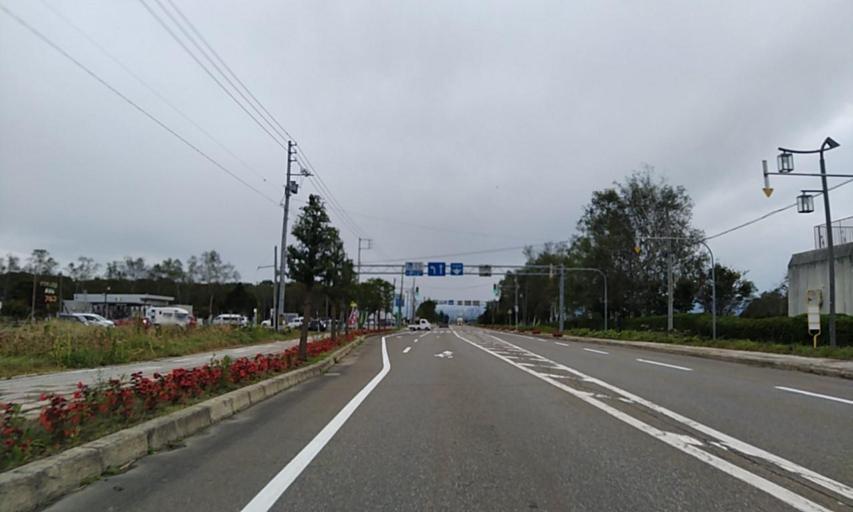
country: JP
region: Hokkaido
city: Obihiro
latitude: 42.5602
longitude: 143.2993
